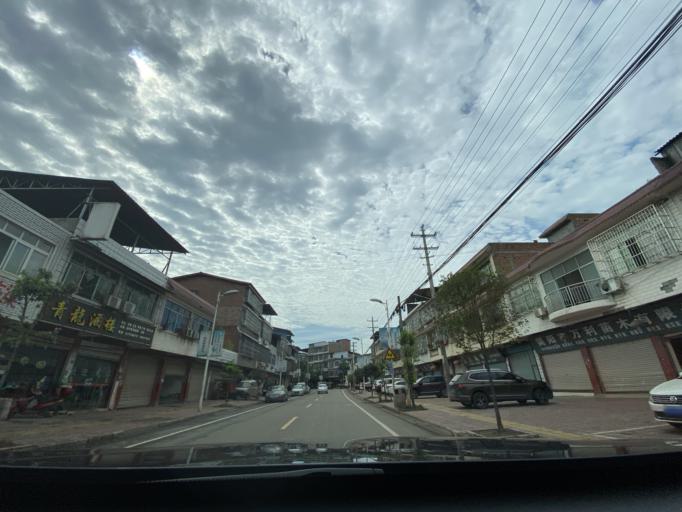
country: CN
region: Sichuan
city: Jiancheng
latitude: 30.4868
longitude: 104.6320
